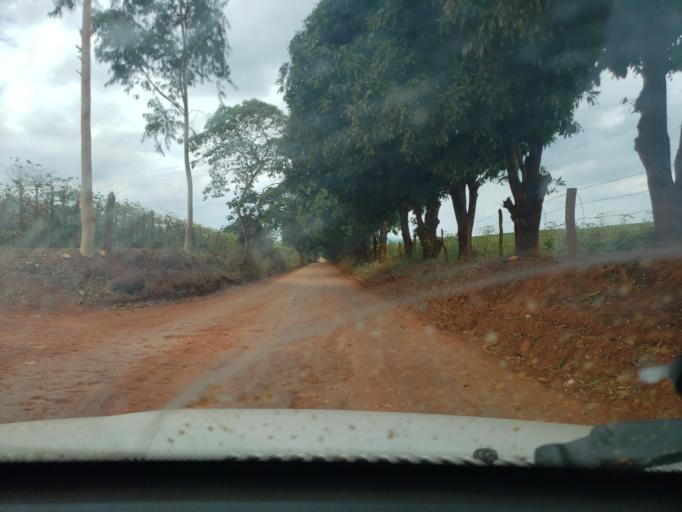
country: BR
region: Minas Gerais
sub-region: Boa Esperanca
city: Boa Esperanca
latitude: -20.9903
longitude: -45.5966
